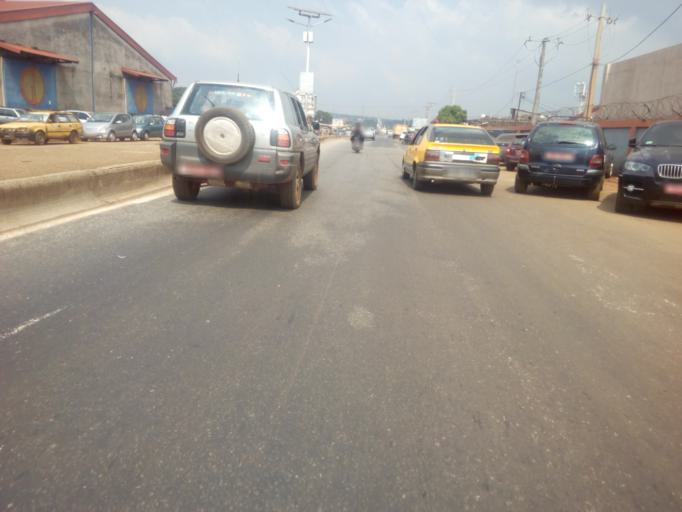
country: GN
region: Conakry
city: Conakry
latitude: 9.6325
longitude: -13.5728
